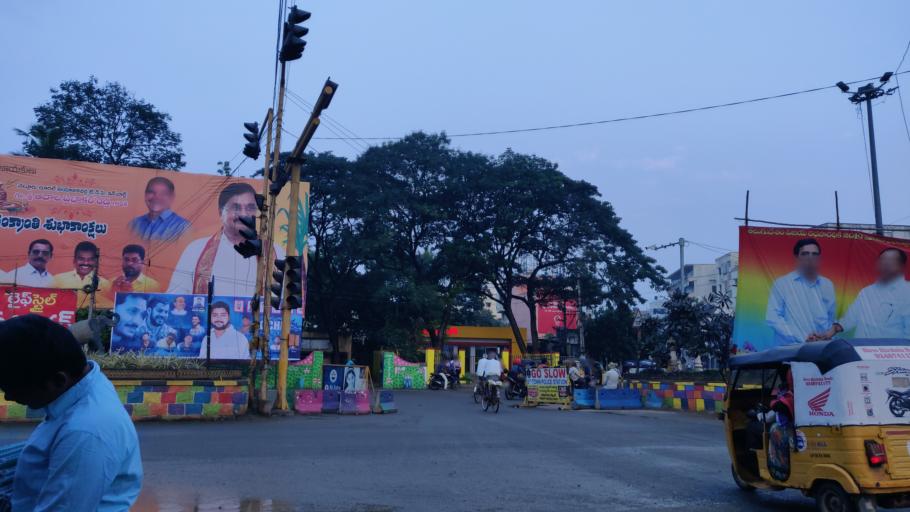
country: IN
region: Andhra Pradesh
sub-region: Nellore
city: Nellore
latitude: 14.4423
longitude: 79.9866
